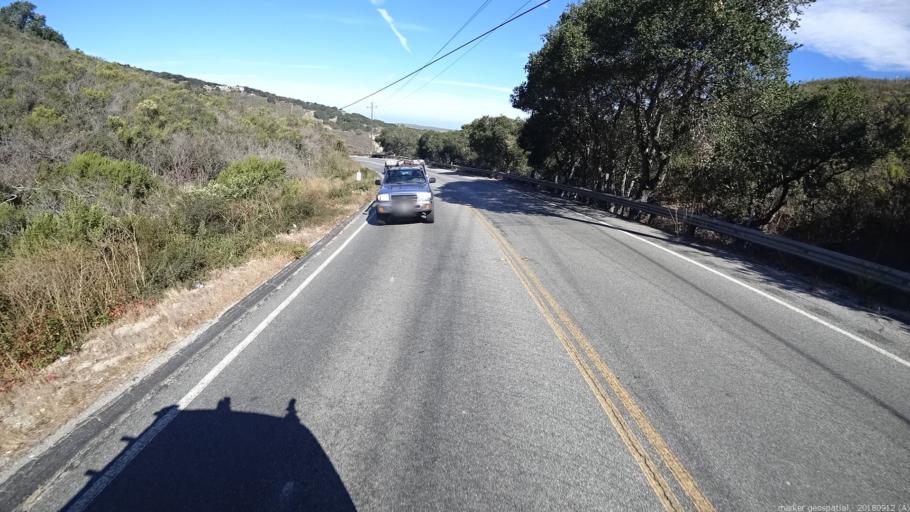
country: US
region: California
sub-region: Monterey County
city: Carmel Valley Village
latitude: 36.5518
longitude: -121.7543
